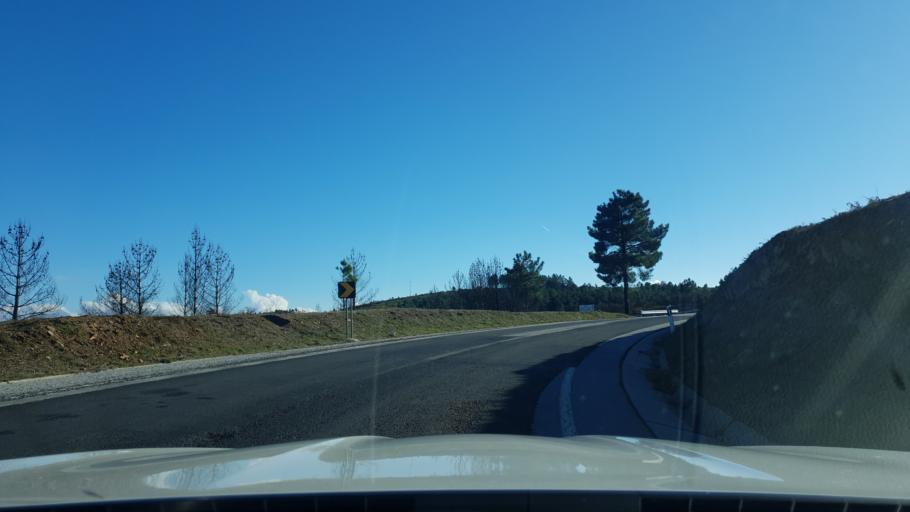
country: PT
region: Braganca
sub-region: Freixo de Espada A Cinta
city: Freixo de Espada a Cinta
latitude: 41.1576
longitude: -6.7987
